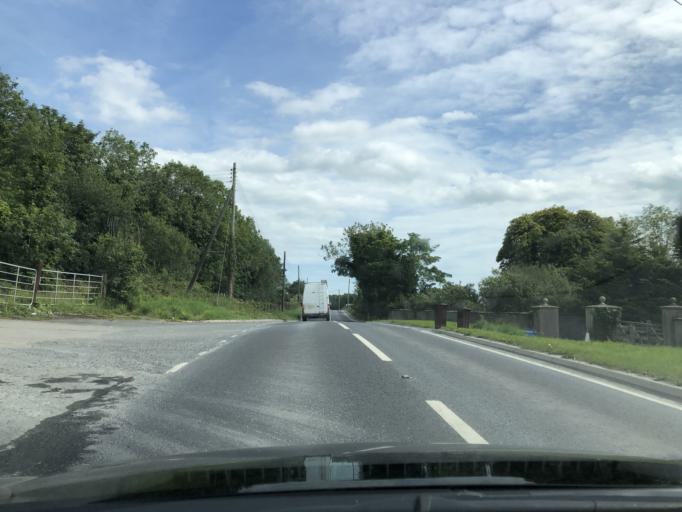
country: GB
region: Northern Ireland
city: Ballynahinch
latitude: 54.4190
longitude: -5.9126
